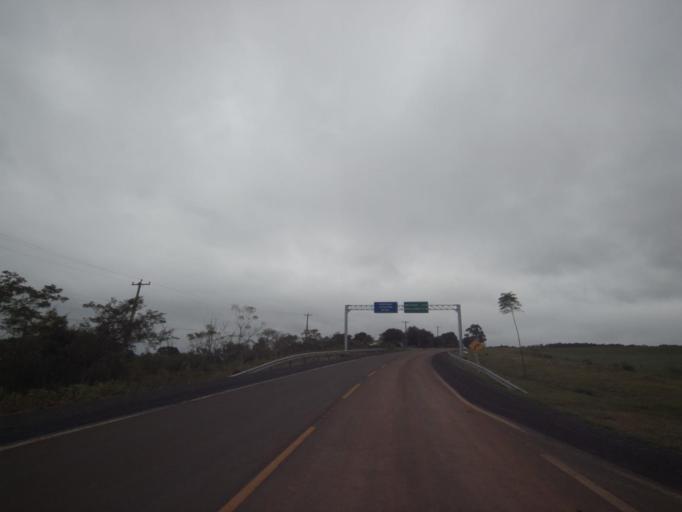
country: AR
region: Misiones
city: El Soberbio
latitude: -27.2901
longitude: -54.1898
